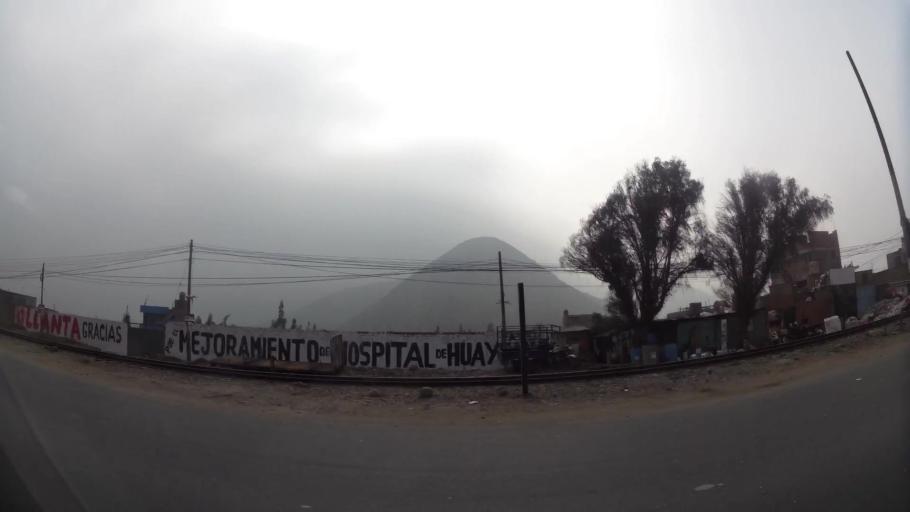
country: PE
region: Lima
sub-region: Lima
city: Santa Maria
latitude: -12.0006
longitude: -76.8396
